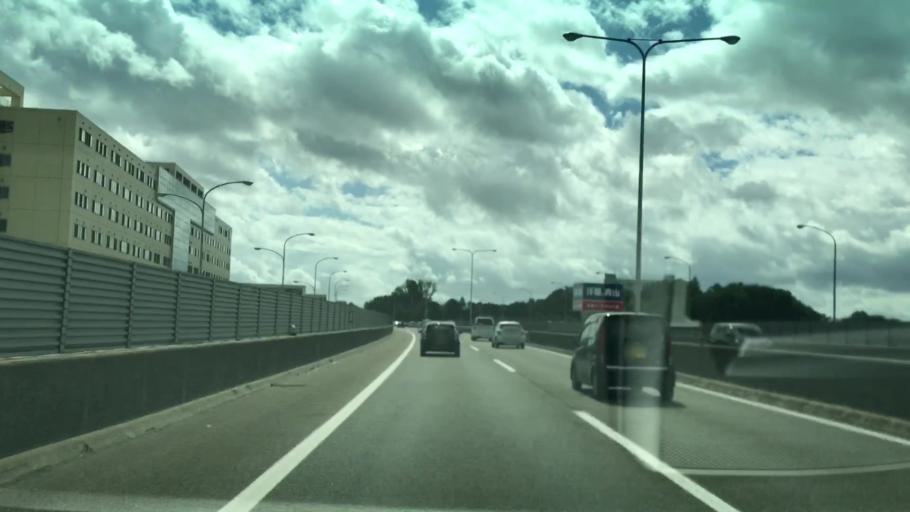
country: JP
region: Hokkaido
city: Sapporo
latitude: 43.0299
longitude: 141.4466
